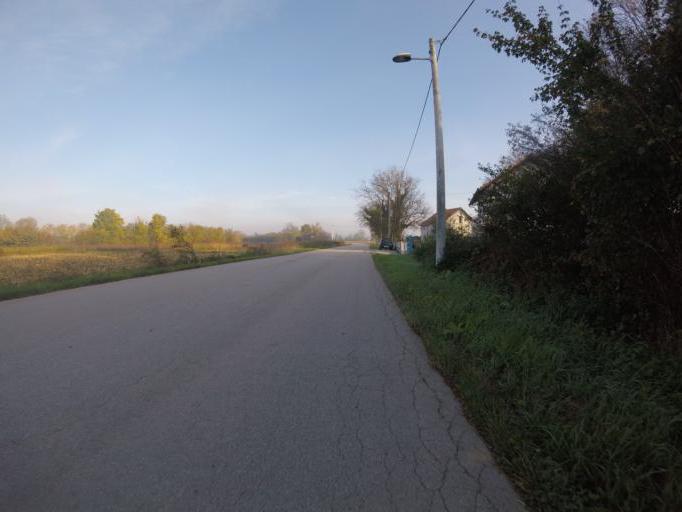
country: HR
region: Zagrebacka
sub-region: Grad Velika Gorica
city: Velika Gorica
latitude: 45.7292
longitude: 16.1144
